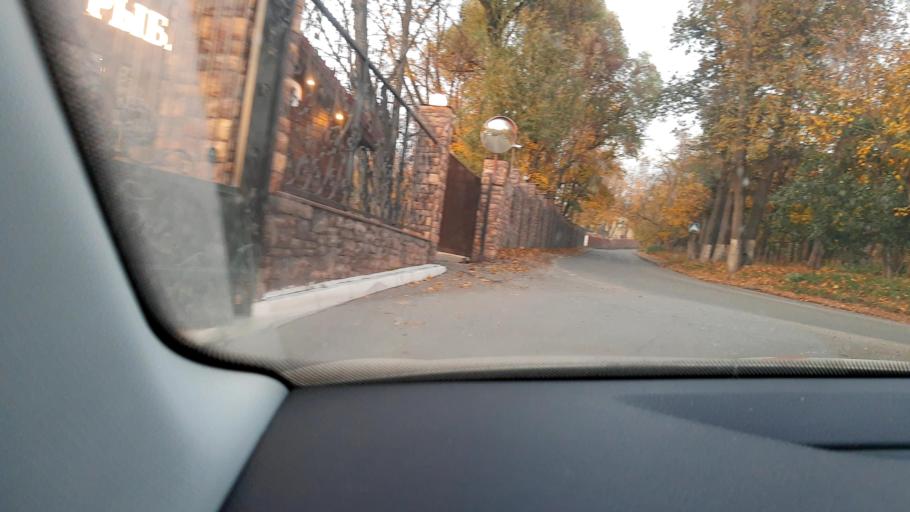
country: RU
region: Moskovskaya
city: Biryulevo Zapadnoye
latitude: 55.5606
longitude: 37.6403
